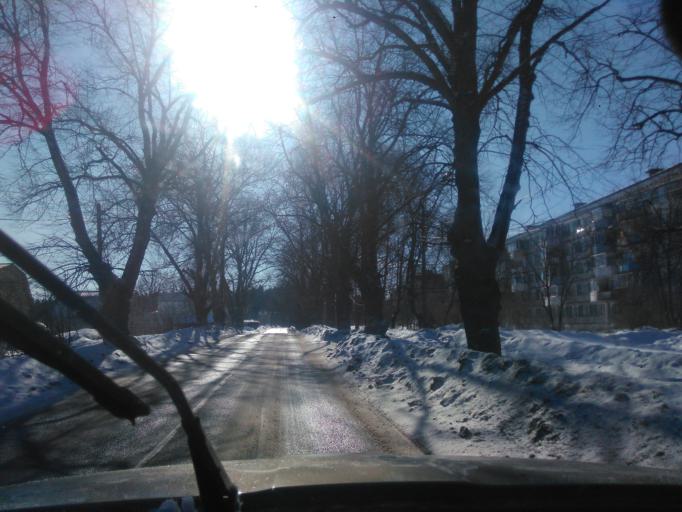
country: RU
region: Moskovskaya
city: Radumlya
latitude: 56.0913
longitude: 37.1517
